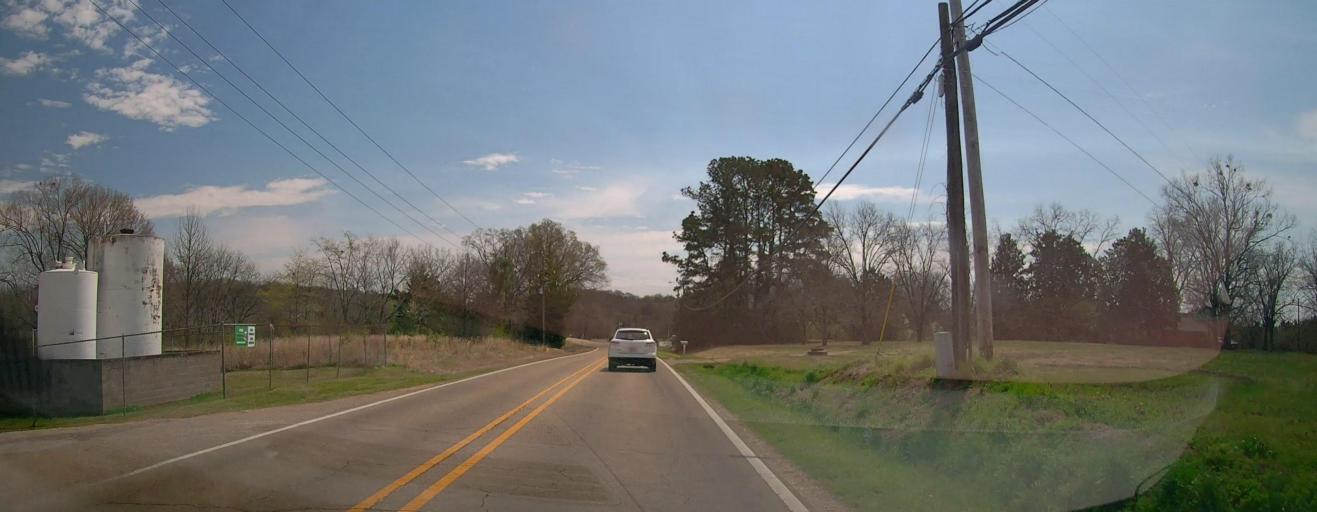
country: US
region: Mississippi
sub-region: Union County
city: New Albany
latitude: 34.4733
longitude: -88.9935
